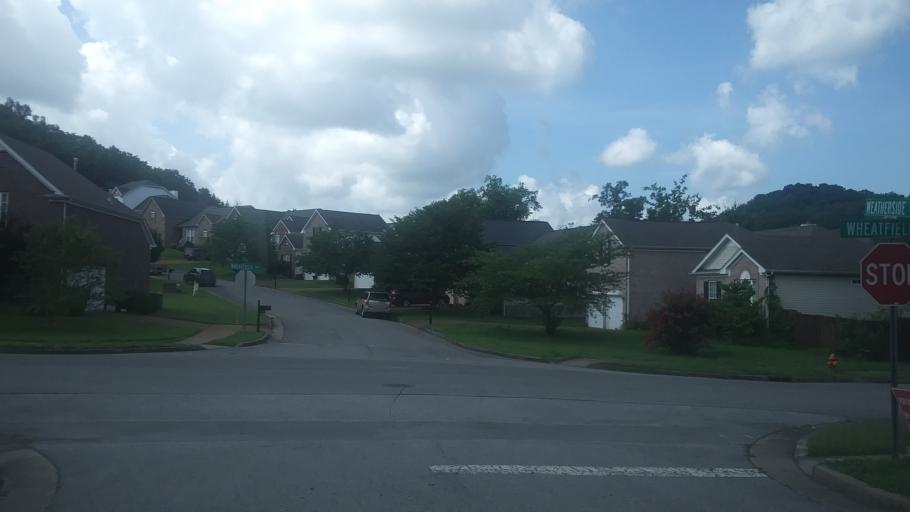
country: US
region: Tennessee
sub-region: Davidson County
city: Belle Meade
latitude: 36.1161
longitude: -86.9314
